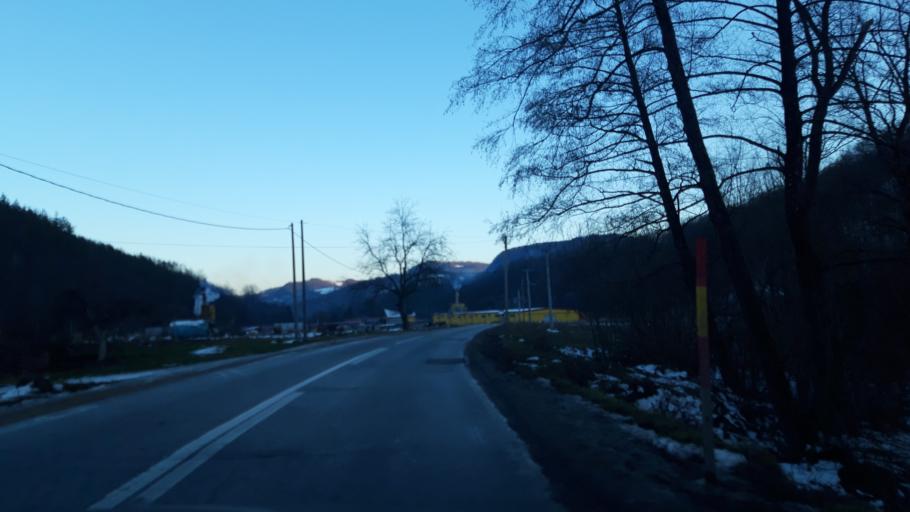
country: BA
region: Republika Srpska
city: Milici
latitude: 44.1672
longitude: 19.0339
